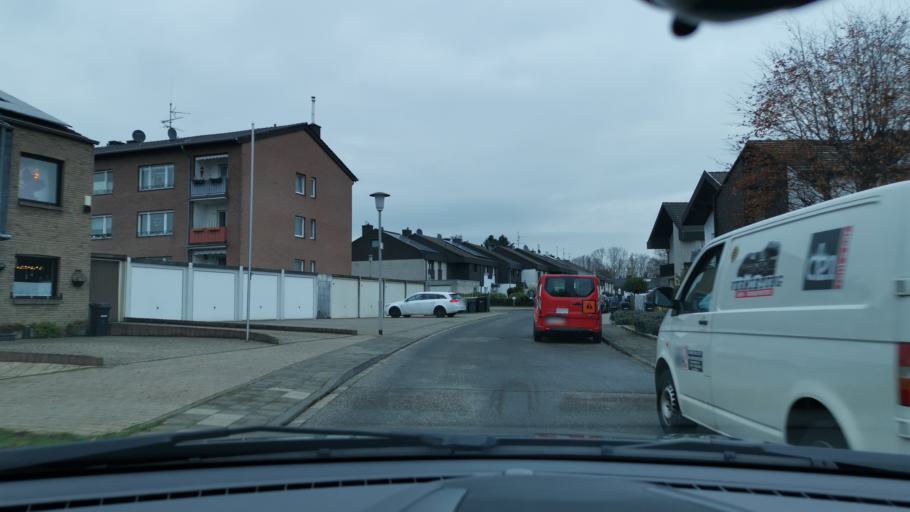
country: DE
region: North Rhine-Westphalia
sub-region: Regierungsbezirk Dusseldorf
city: Neubrueck
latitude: 51.1327
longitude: 6.6279
